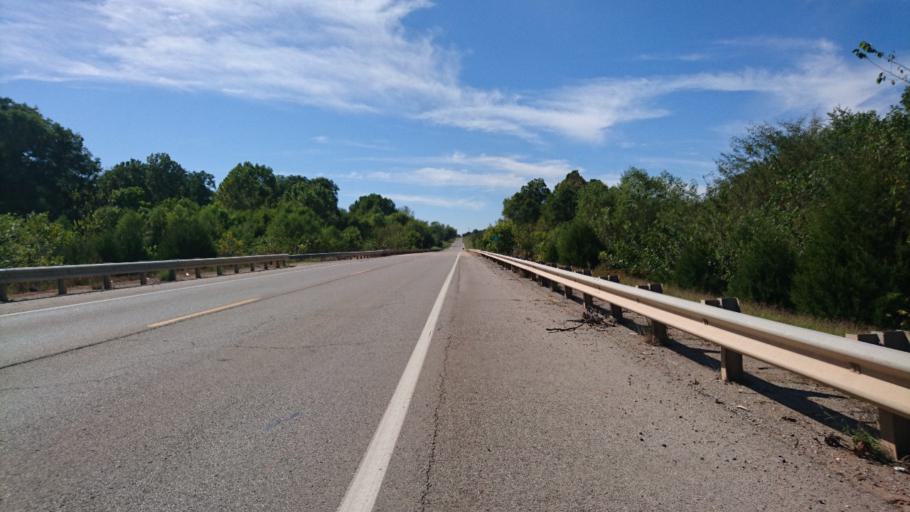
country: US
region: Oklahoma
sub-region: Lincoln County
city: Stroud
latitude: 35.7241
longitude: -96.7433
